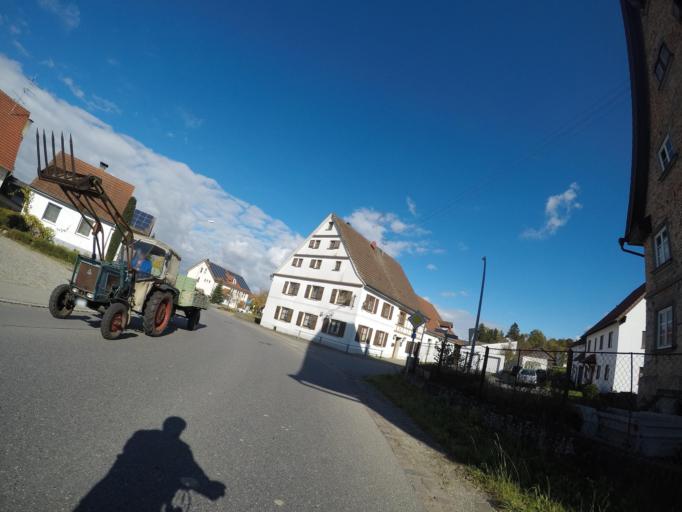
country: DE
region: Baden-Wuerttemberg
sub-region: Tuebingen Region
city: Grundsheim
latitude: 48.1485
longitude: 9.6668
